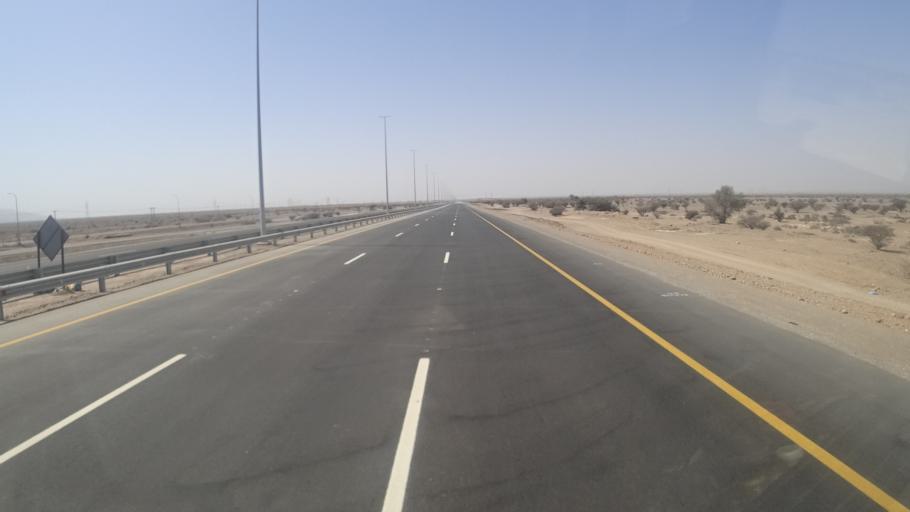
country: OM
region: Ash Sharqiyah
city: Sur
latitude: 22.3012
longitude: 59.2826
